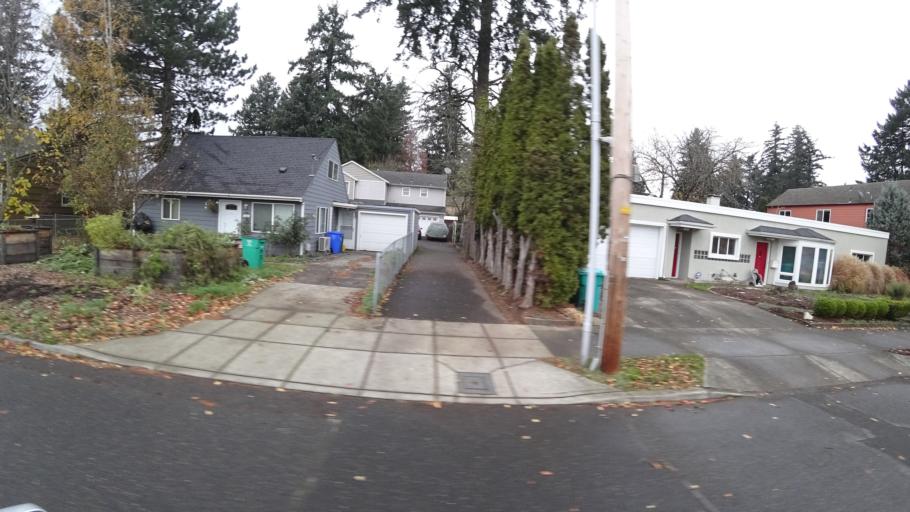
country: US
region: Oregon
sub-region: Multnomah County
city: Lents
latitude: 45.5299
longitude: -122.5544
